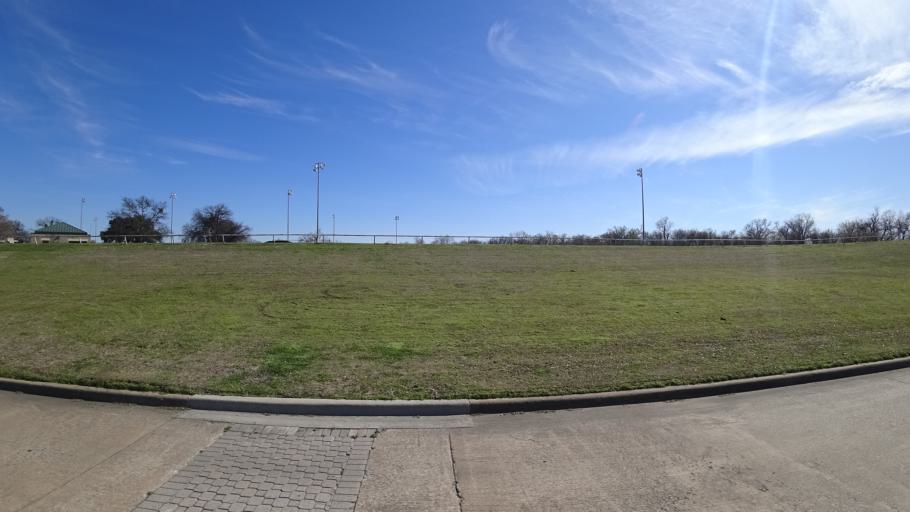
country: US
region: Texas
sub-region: Dallas County
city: Coppell
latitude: 32.9892
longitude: -96.9626
